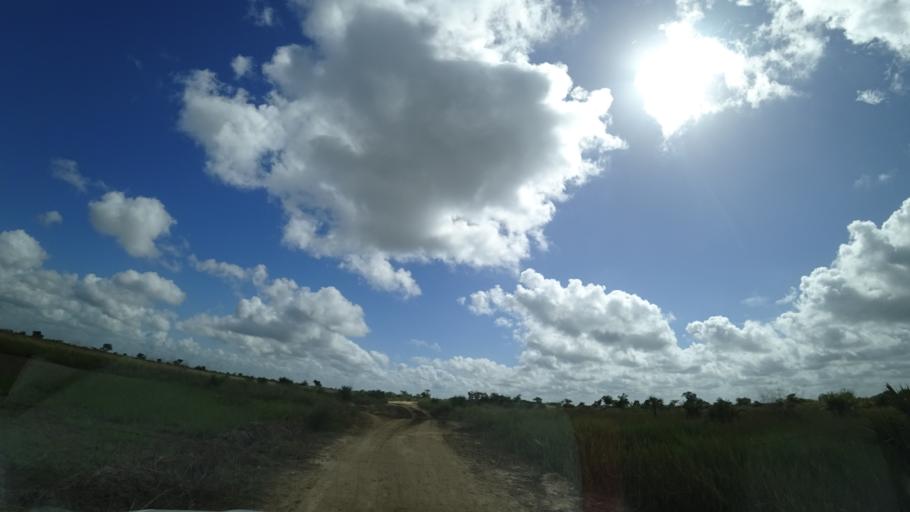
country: MZ
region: Sofala
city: Dondo
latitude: -19.4099
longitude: 34.5662
